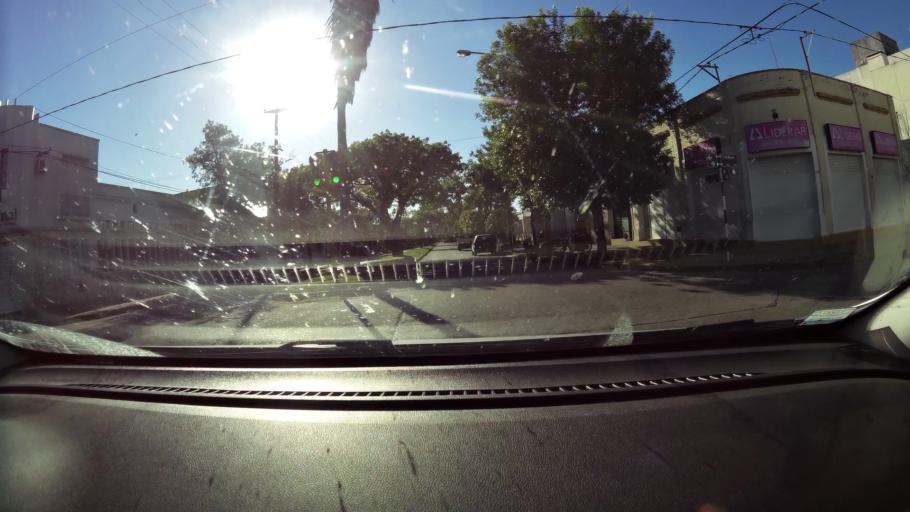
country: AR
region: Cordoba
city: San Francisco
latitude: -31.4372
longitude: -62.0765
